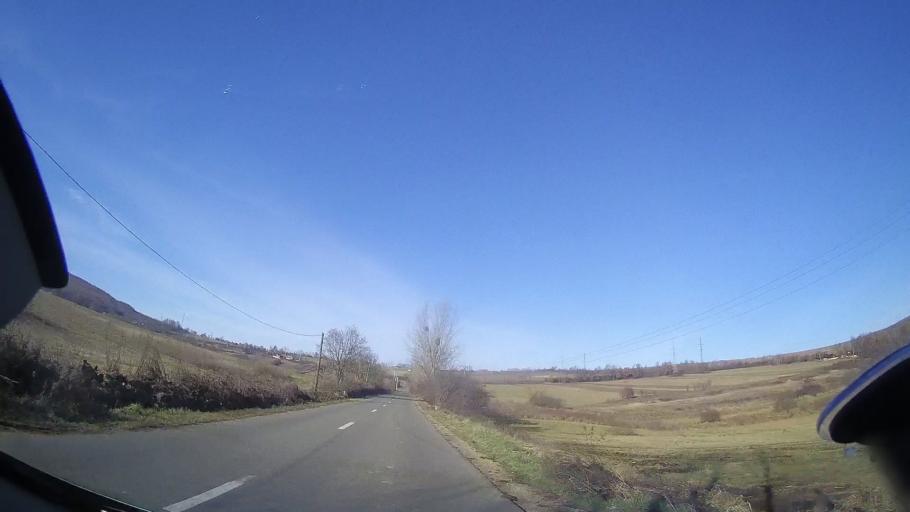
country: RO
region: Bihor
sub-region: Comuna Suncuius
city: Balnaca
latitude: 46.9672
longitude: 22.5503
